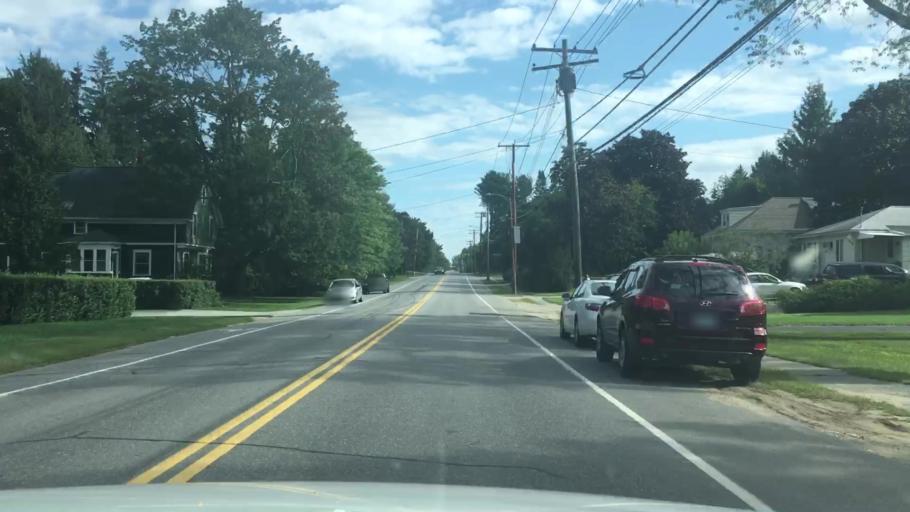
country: US
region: Maine
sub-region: Androscoggin County
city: Lewiston
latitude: 44.1136
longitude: -70.1991
